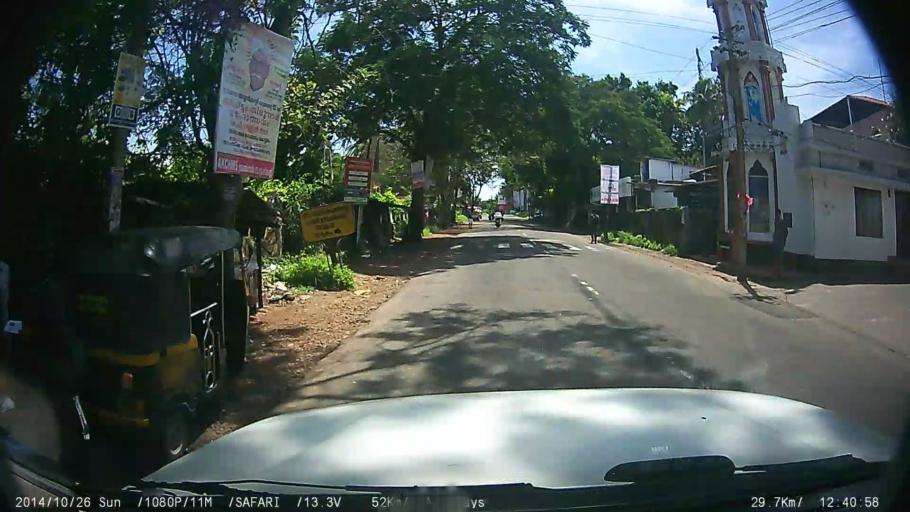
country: IN
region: Kerala
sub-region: Kottayam
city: Kottayam
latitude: 9.5530
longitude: 76.5129
